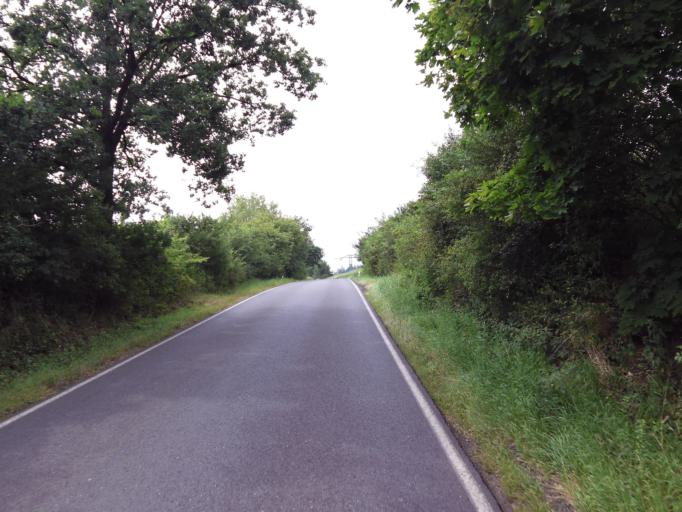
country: CZ
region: Central Bohemia
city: Tynec nad Sazavou
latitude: 49.8662
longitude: 14.5848
